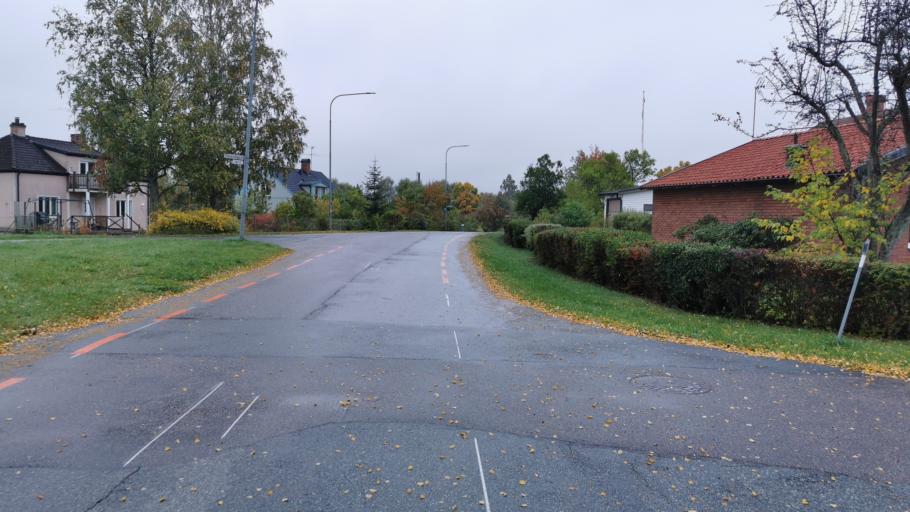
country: SE
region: OErebro
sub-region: Orebro Kommun
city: Hovsta
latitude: 59.3145
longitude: 15.2275
